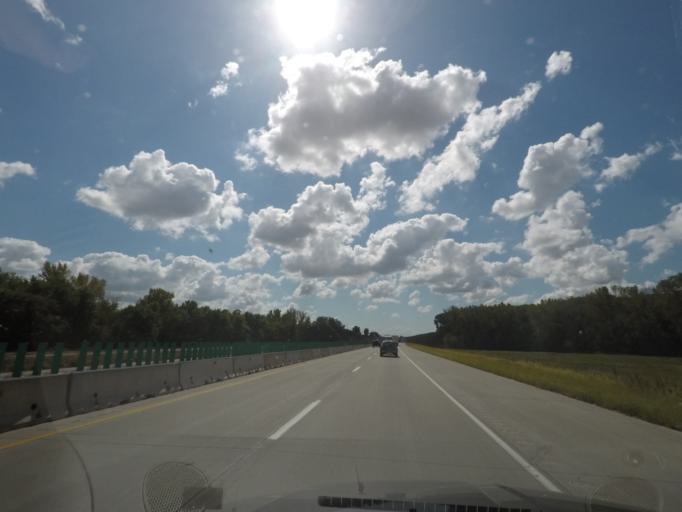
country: US
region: Iowa
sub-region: Story County
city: Huxley
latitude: 41.9588
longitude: -93.5701
